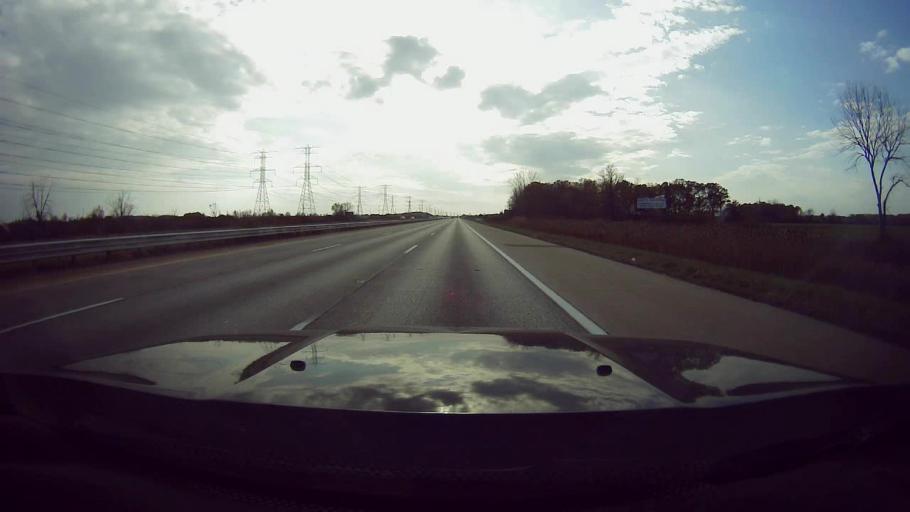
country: US
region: Michigan
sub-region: Monroe County
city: South Rockwood
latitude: 42.0334
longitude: -83.2907
